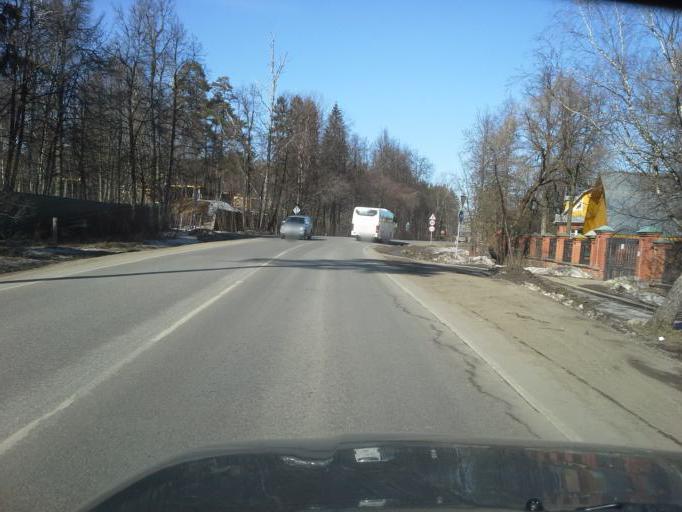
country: RU
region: Moskovskaya
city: Lesnoy Gorodok
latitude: 55.6680
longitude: 37.1745
